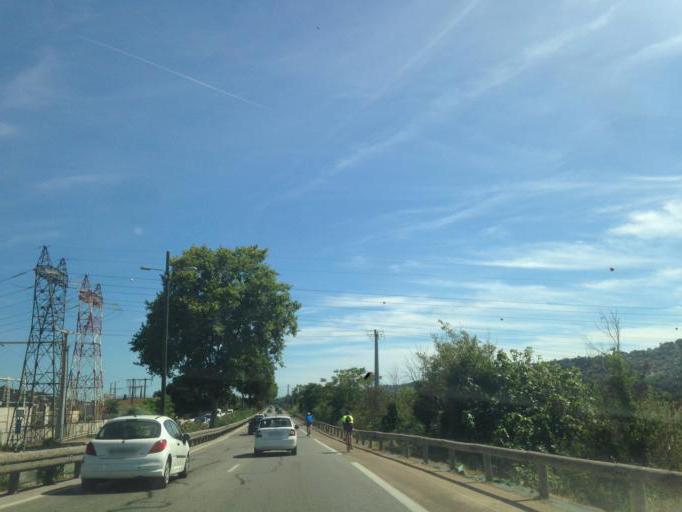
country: FR
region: Provence-Alpes-Cote d'Azur
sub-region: Departement des Alpes-Maritimes
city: La Gaude
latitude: 43.7205
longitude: 7.1862
